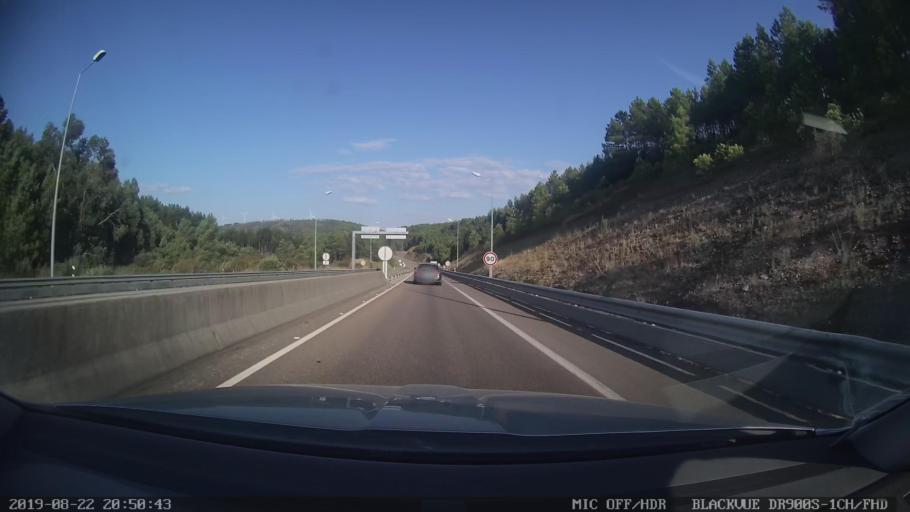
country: PT
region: Castelo Branco
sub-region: Proenca-A-Nova
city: Proenca-a-Nova
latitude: 39.7568
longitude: -7.9442
